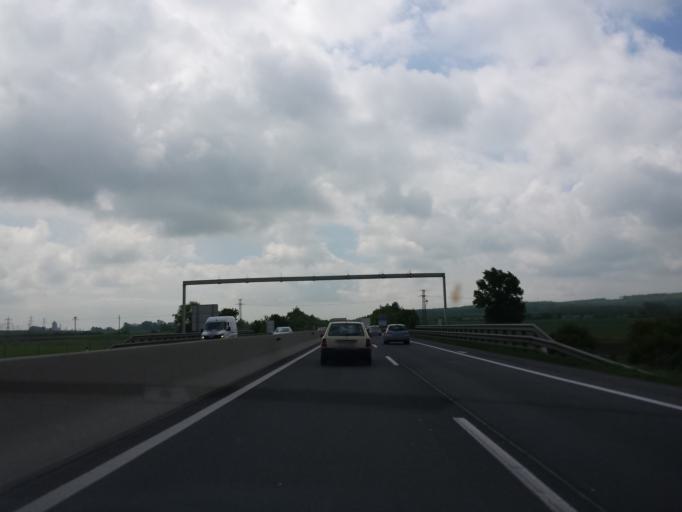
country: AT
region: Burgenland
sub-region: Politischer Bezirk Neusiedl am See
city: Parndorf
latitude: 48.0122
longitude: 16.8360
